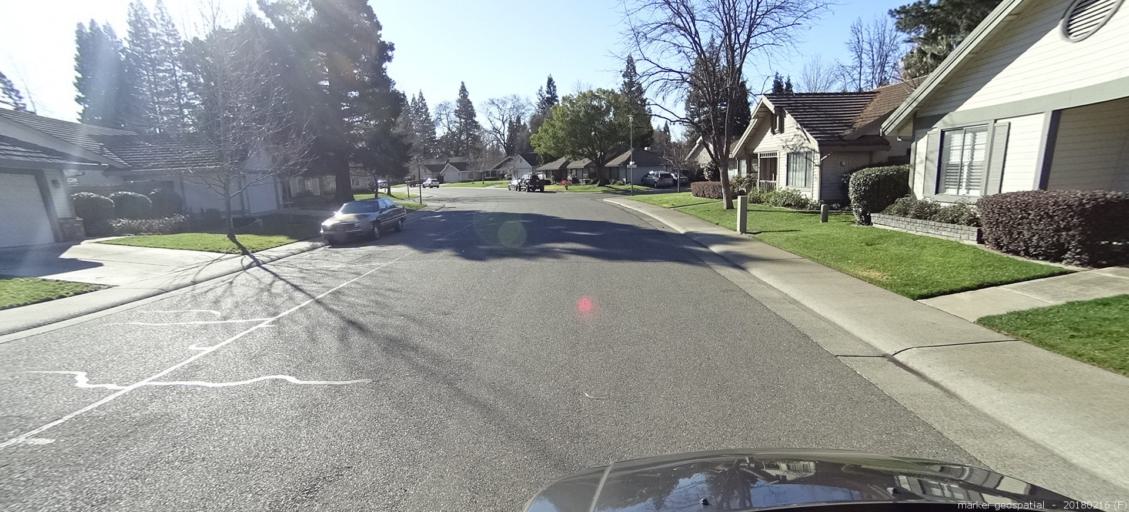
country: US
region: California
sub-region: Sacramento County
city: Gold River
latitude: 38.6258
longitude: -121.2479
